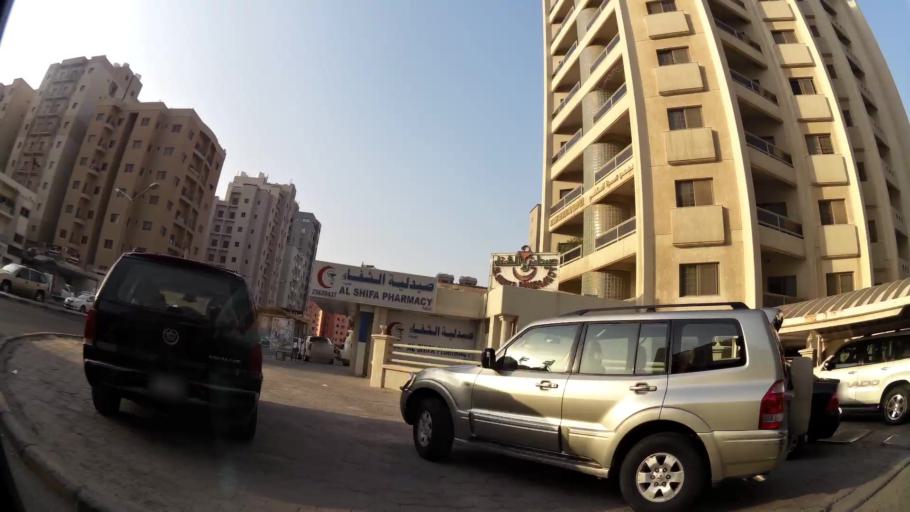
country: KW
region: Muhafazat Hawalli
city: As Salimiyah
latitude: 29.3290
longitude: 48.0556
